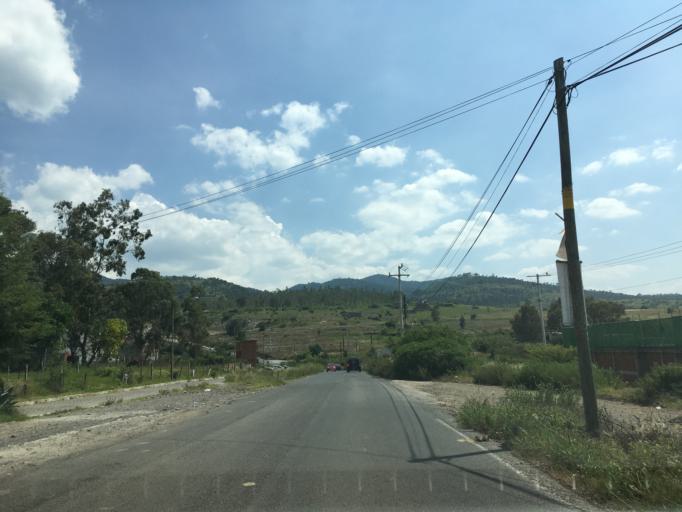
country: MX
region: Michoacan
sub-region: Morelia
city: Morelos
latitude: 19.6534
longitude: -101.2027
